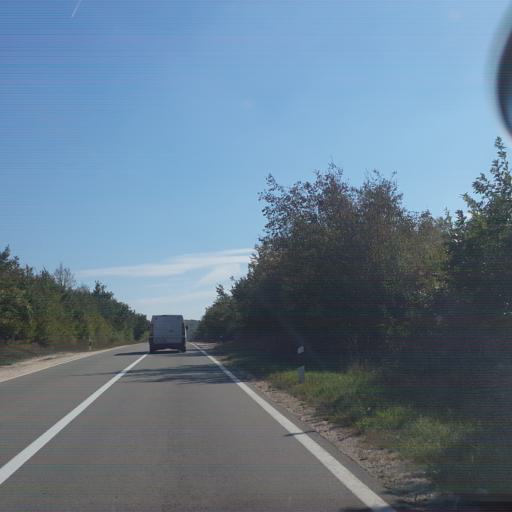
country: RS
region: Central Serbia
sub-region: Zajecarski Okrug
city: Knjazevac
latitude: 43.5004
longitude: 22.2170
